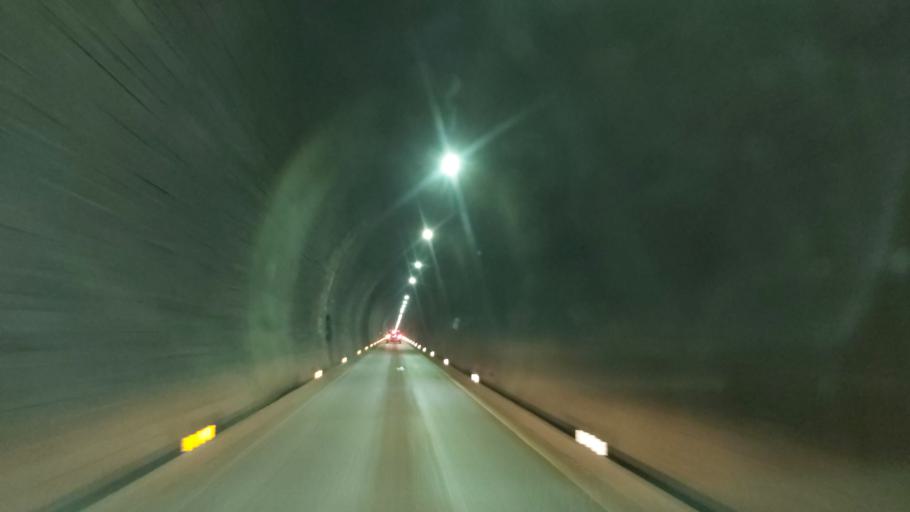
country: CL
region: Araucania
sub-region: Provincia de Cautin
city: Vilcun
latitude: -38.5331
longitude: -71.5095
